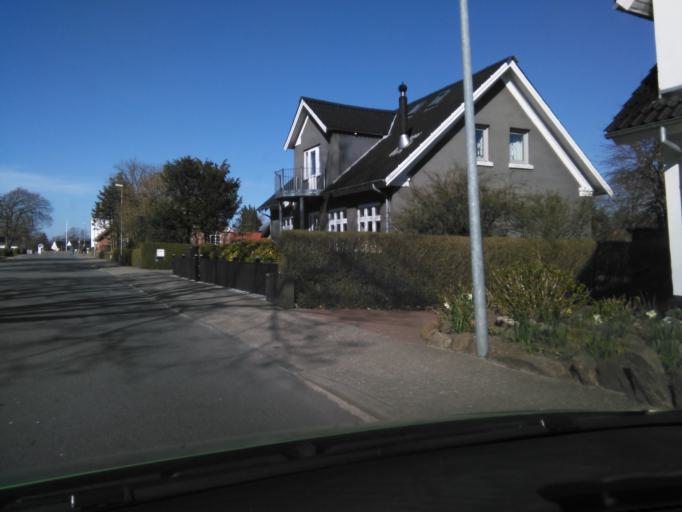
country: DK
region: South Denmark
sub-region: Varde Kommune
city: Oksbol
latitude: 55.6296
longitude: 8.2796
